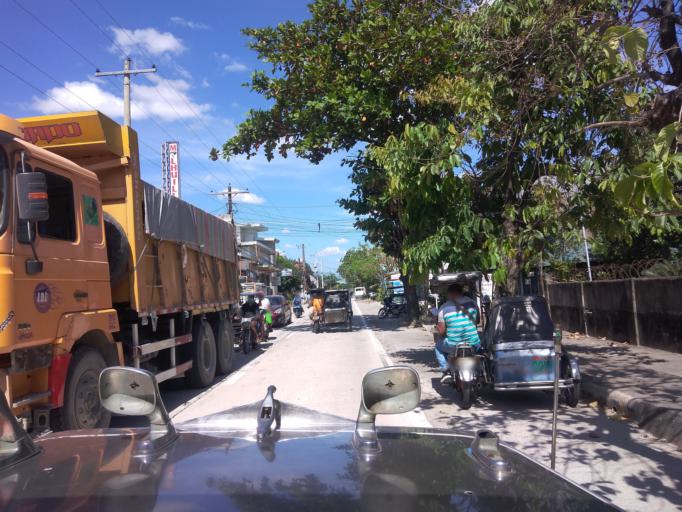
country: PH
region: Central Luzon
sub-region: Province of Pampanga
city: Santa Rita
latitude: 14.9987
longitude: 120.6132
